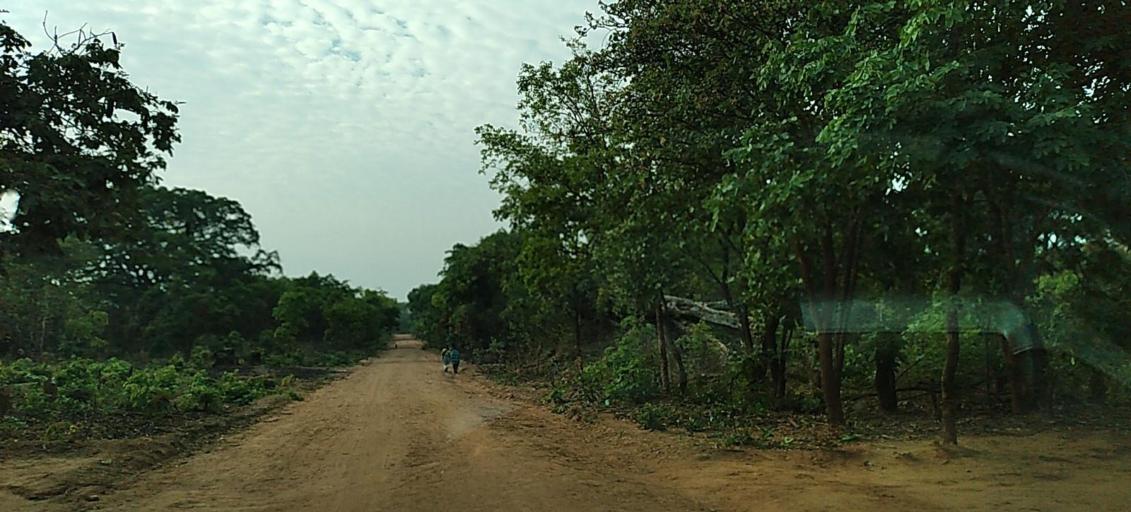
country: ZM
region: Copperbelt
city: Kalulushi
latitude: -12.9055
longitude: 27.6877
